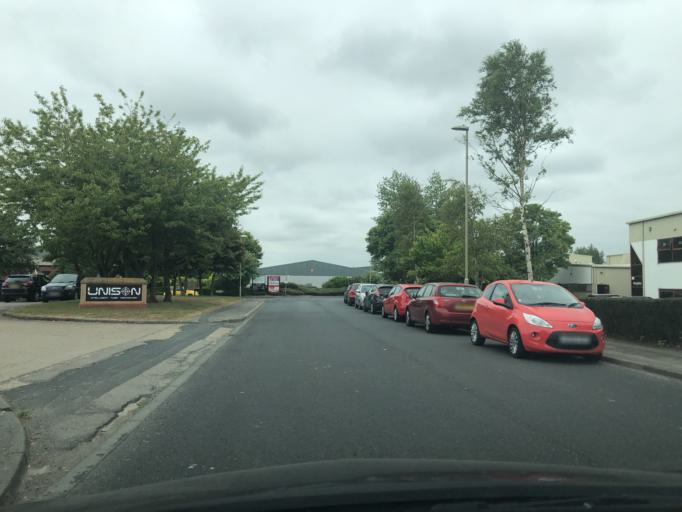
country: GB
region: England
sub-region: North Yorkshire
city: Scarborough
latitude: 54.2381
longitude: -0.4081
